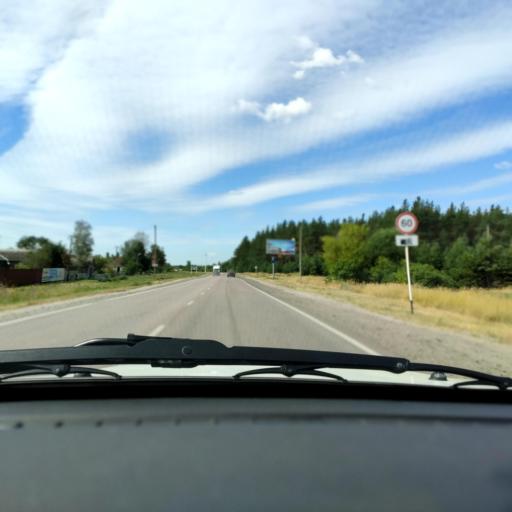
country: RU
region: Voronezj
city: Uglyanets
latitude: 51.8540
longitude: 39.6644
